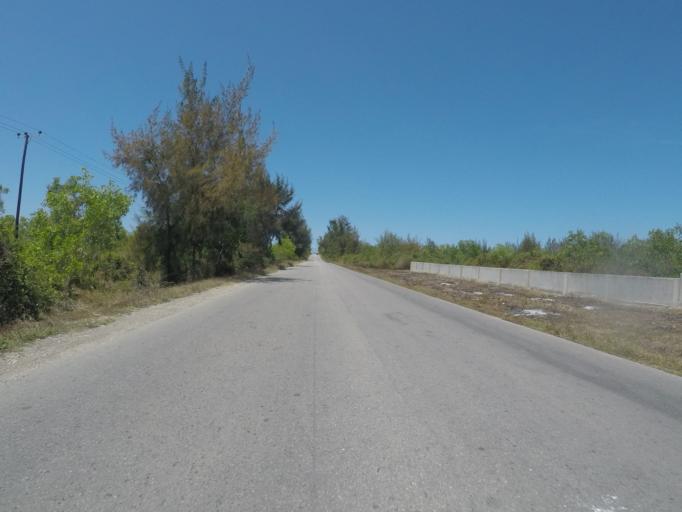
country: TZ
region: Zanzibar Central/South
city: Nganane
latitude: -6.2694
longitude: 39.5137
